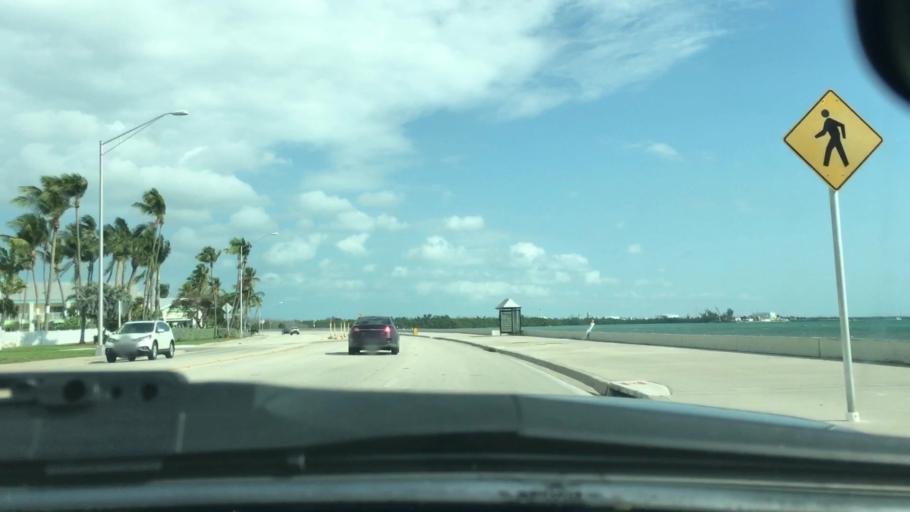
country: US
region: Florida
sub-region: Monroe County
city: Stock Island
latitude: 24.5538
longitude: -81.7499
